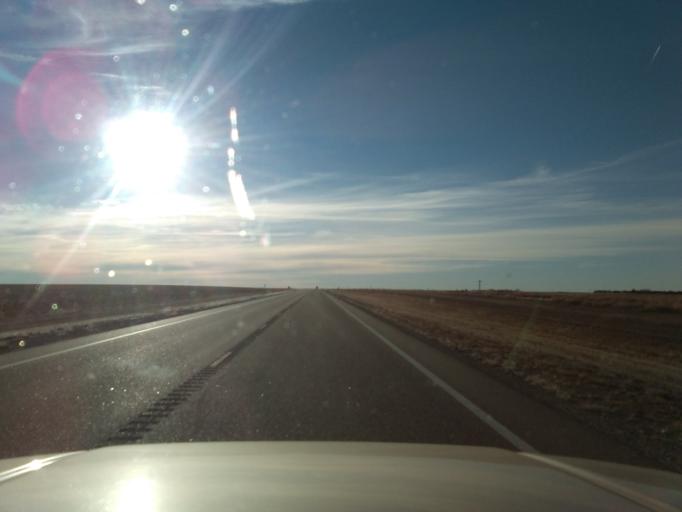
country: US
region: Kansas
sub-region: Sheridan County
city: Hoxie
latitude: 39.5173
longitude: -100.6299
